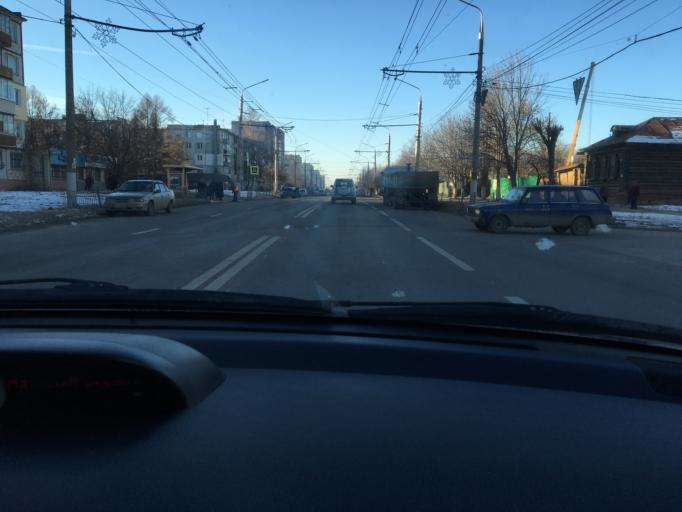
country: RU
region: Tula
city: Tula
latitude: 54.2194
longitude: 37.6145
